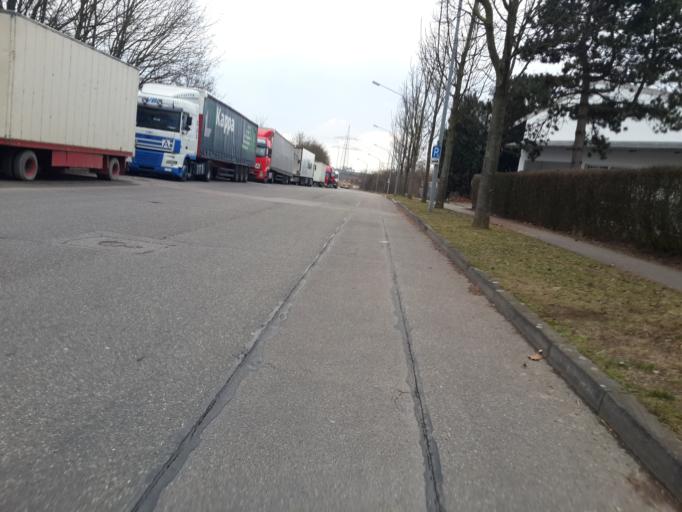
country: DE
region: Baden-Wuerttemberg
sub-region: Regierungsbezirk Stuttgart
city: Untereisesheim
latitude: 49.1824
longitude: 9.1840
